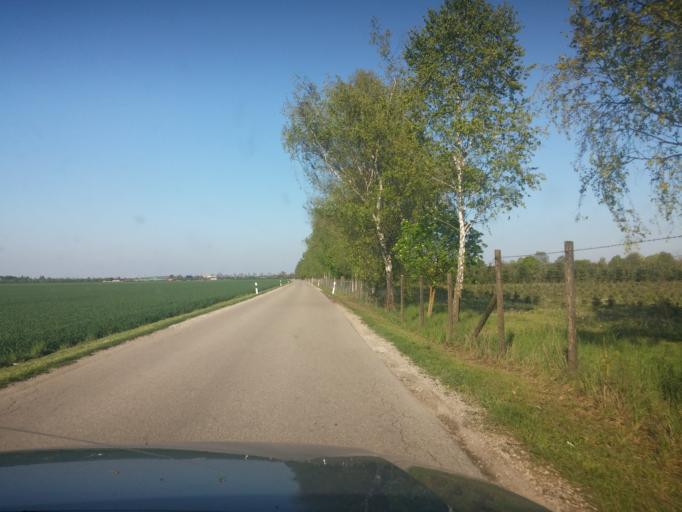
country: DE
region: Bavaria
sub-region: Upper Bavaria
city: Feldkirchen
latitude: 48.1302
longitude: 11.7442
